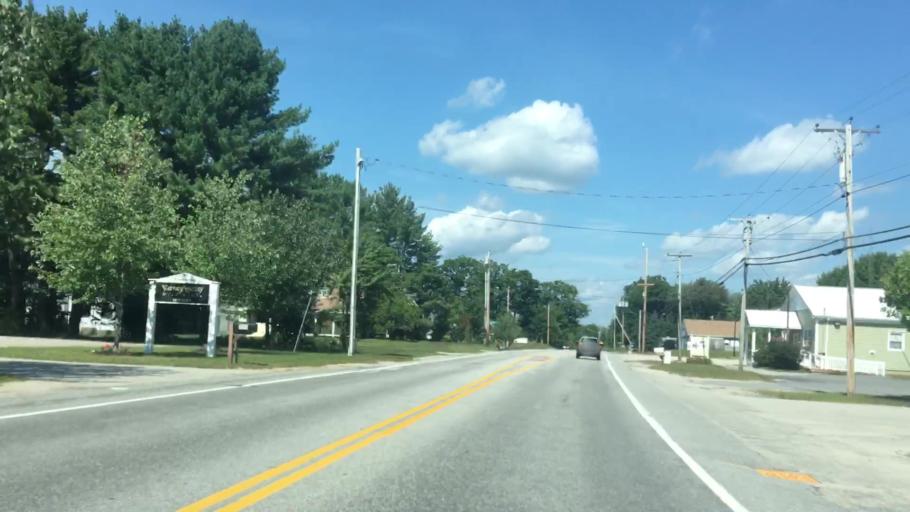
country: US
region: Maine
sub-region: Cumberland County
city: New Gloucester
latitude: 43.8955
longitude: -70.3280
